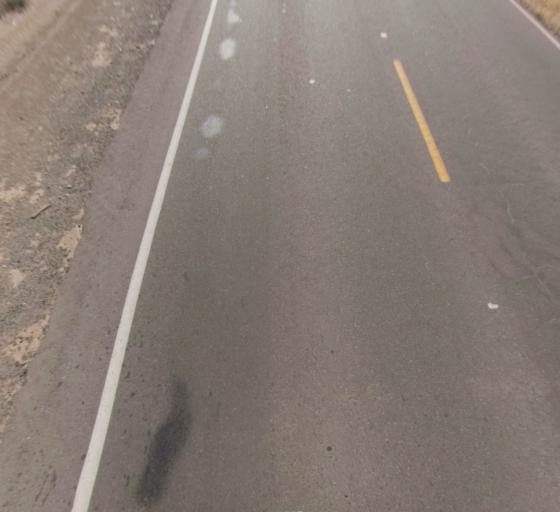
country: US
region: California
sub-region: Fresno County
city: Biola
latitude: 36.8514
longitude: -120.0146
